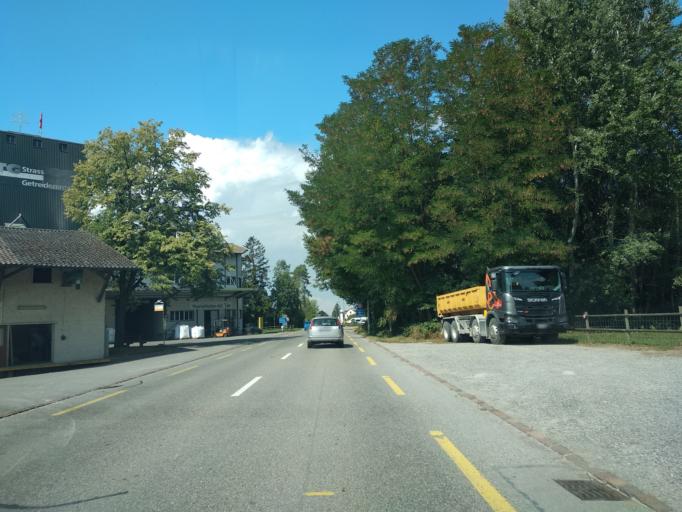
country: CH
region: Thurgau
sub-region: Frauenfeld District
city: Gachnang
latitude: 47.5664
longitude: 8.8600
